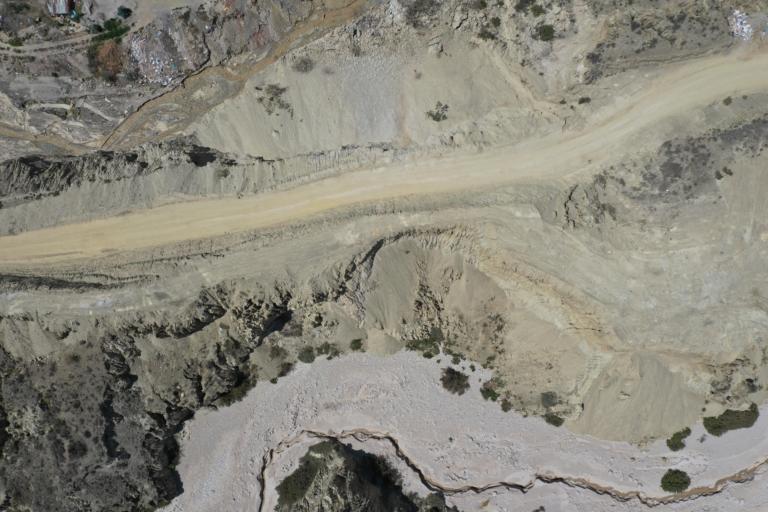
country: BO
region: La Paz
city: La Paz
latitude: -16.5632
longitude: -68.1143
